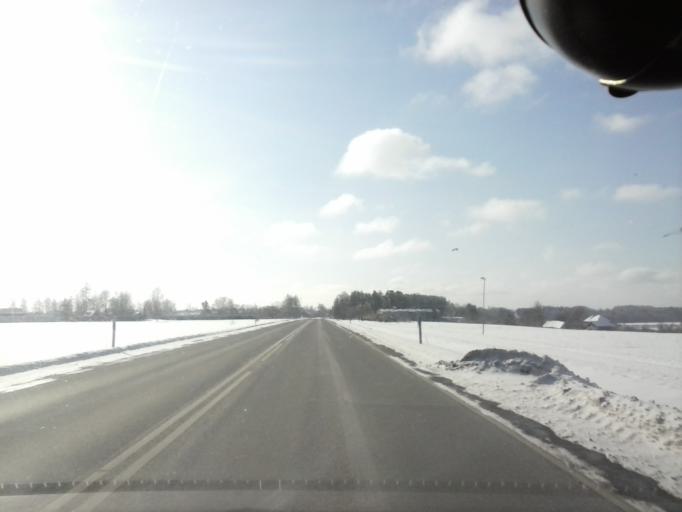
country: EE
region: Viljandimaa
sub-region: Viiratsi vald
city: Viiratsi
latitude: 58.3724
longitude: 25.6497
